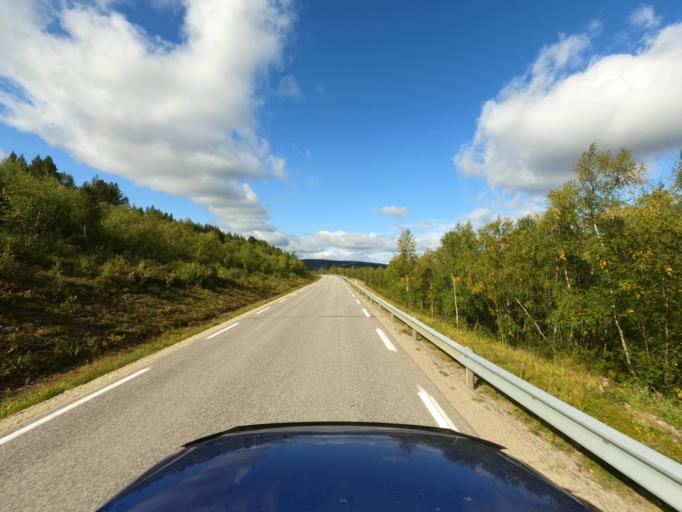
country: NO
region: Finnmark Fylke
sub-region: Karasjok
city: Karasjohka
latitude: 69.4537
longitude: 25.5739
